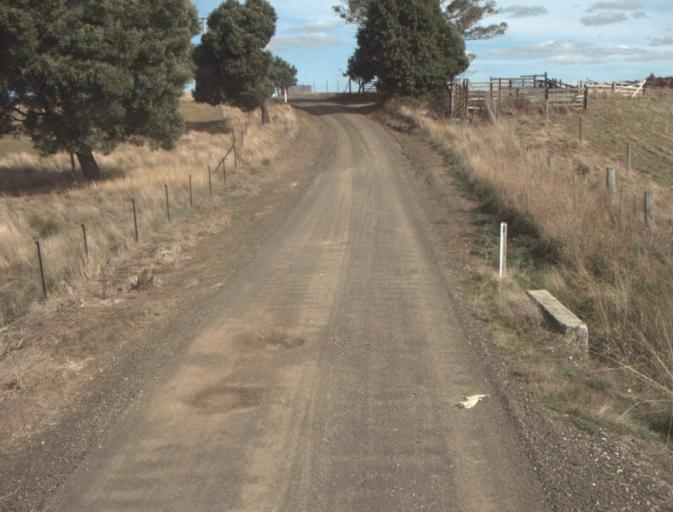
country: AU
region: Tasmania
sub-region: Launceston
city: Mayfield
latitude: -41.1874
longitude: 147.1910
